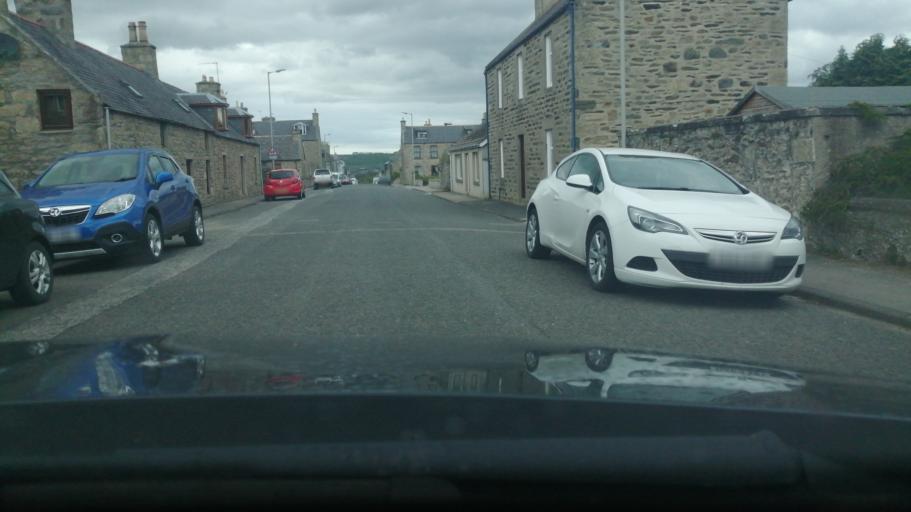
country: GB
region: Scotland
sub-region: Moray
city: Keith
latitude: 57.5376
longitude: -2.9527
